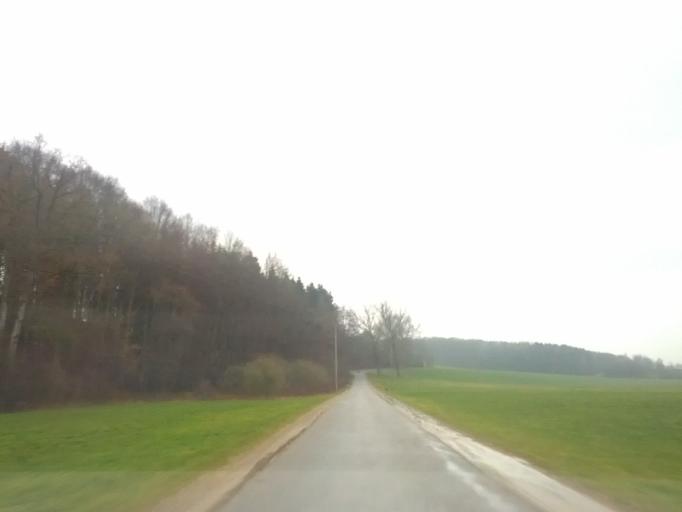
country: DE
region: Baden-Wuerttemberg
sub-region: Tuebingen Region
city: Rot an der Rot
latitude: 47.9946
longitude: 10.0004
